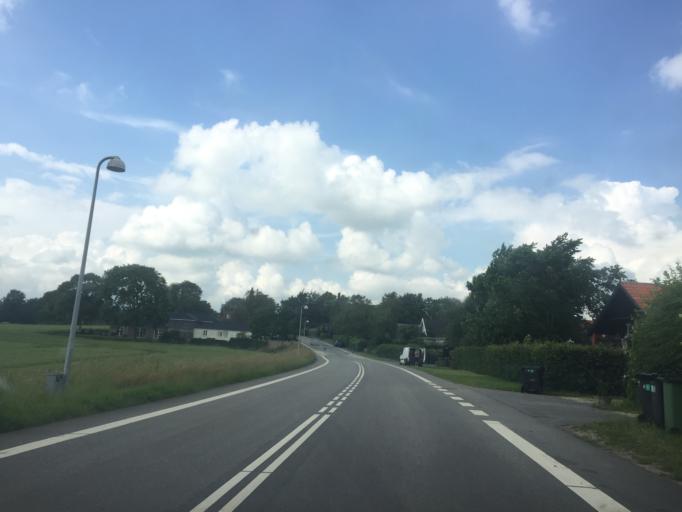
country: DK
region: Zealand
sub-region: Roskilde Kommune
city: Gundsomagle
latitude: 55.7049
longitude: 12.1625
